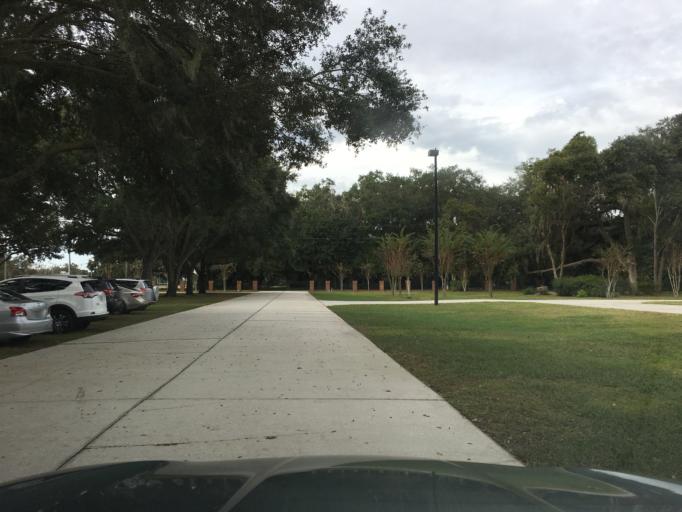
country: US
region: Florida
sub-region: Hillsborough County
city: Plant City
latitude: 28.0377
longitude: -82.1082
